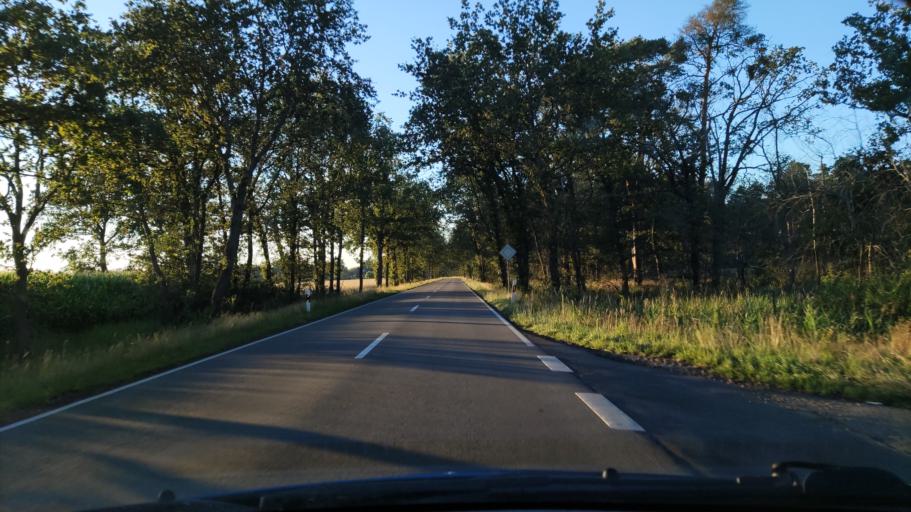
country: DE
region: Lower Saxony
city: Klein Gusborn
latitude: 53.0425
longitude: 11.1776
